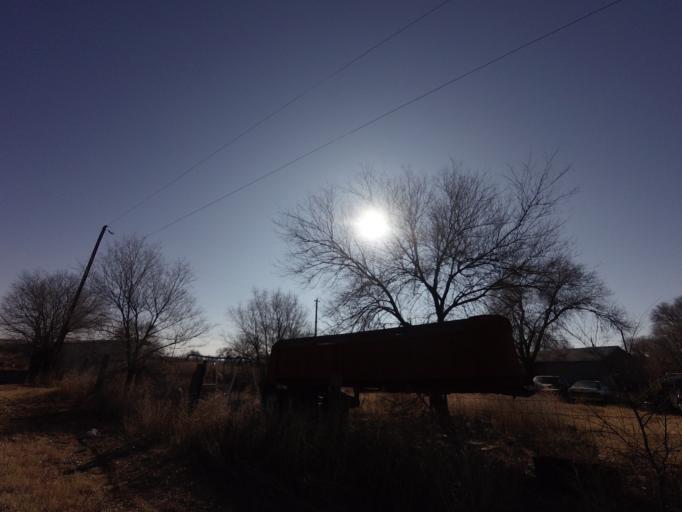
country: US
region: New Mexico
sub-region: Curry County
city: Clovis
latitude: 34.3854
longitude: -103.1832
